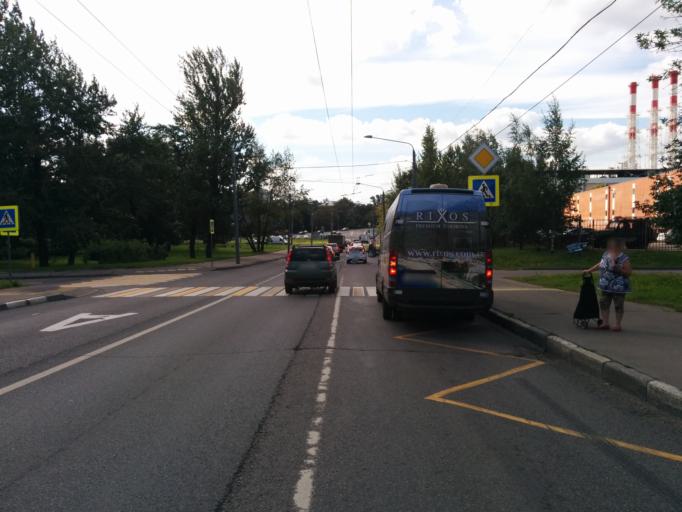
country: RU
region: Moscow
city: Mar'ina Roshcha
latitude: 55.8143
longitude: 37.6182
